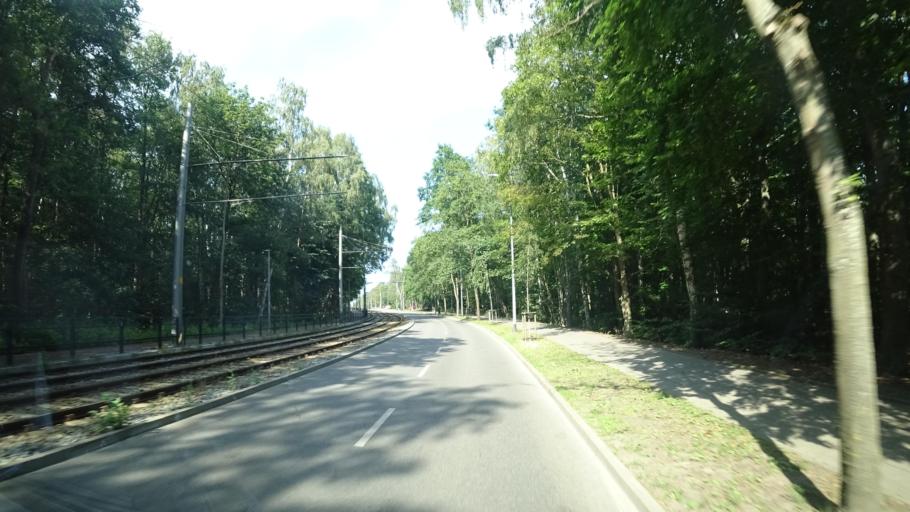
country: PL
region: Pomeranian Voivodeship
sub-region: Gdansk
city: Gdansk
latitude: 54.3663
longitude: 18.7238
